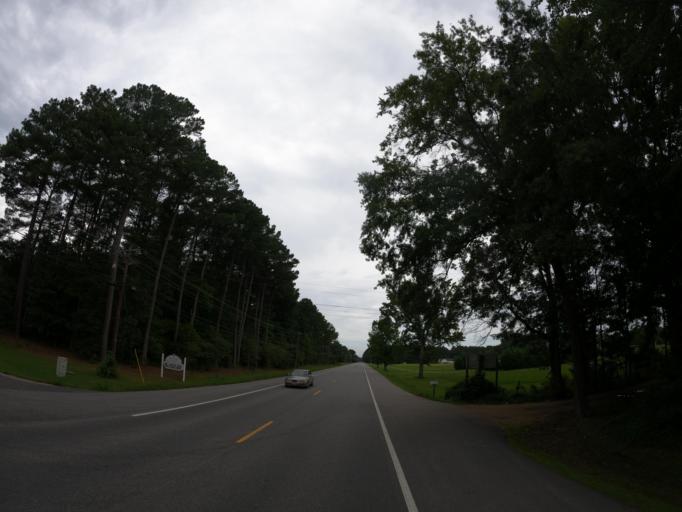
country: US
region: Maryland
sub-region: Saint Mary's County
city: Lexington Park
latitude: 38.1537
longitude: -76.5172
